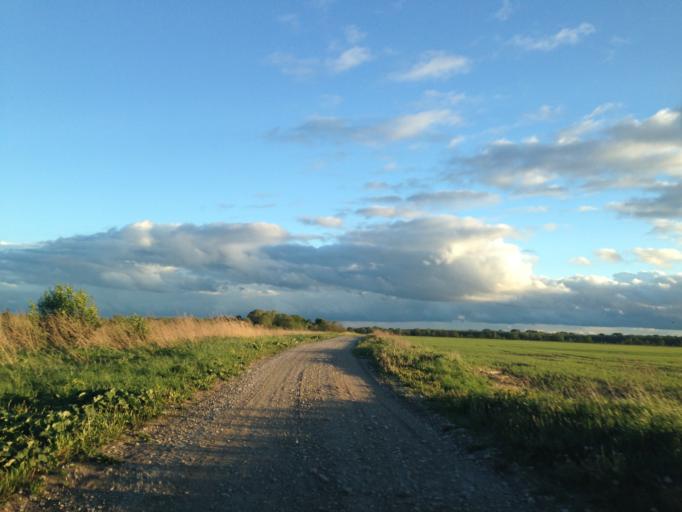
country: EE
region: Raplamaa
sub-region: Maerjamaa vald
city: Marjamaa
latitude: 58.7561
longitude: 24.1806
